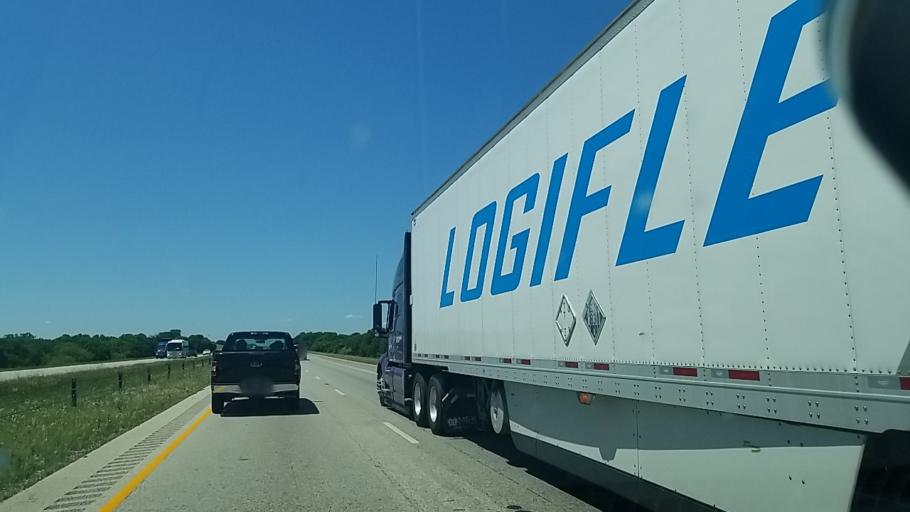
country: US
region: Texas
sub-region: Leon County
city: Buffalo
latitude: 31.4294
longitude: -96.0564
